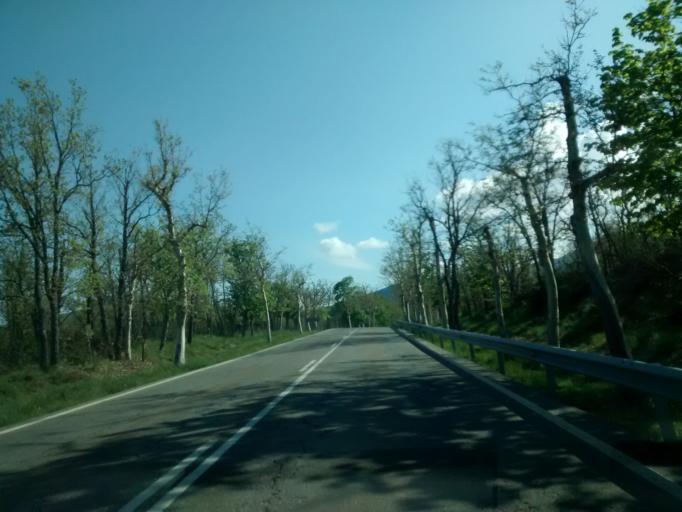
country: ES
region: Castille and Leon
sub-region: Provincia de Segovia
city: San Ildefonso
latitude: 40.8893
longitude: -4.0145
